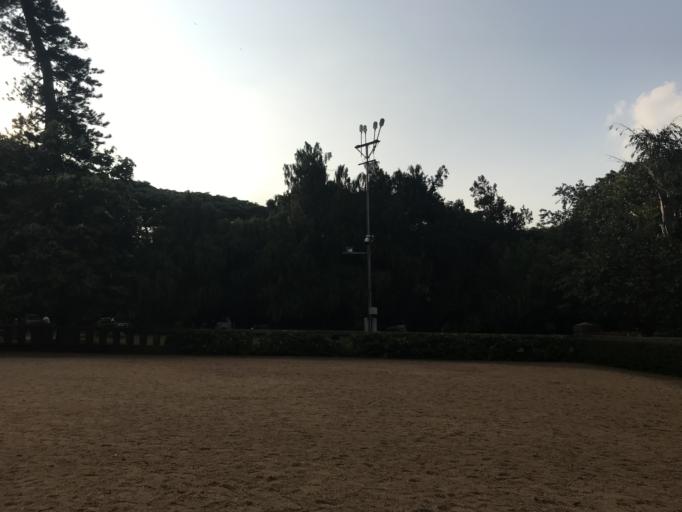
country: IN
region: Karnataka
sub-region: Bangalore Urban
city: Bangalore
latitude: 13.0173
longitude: 77.5670
